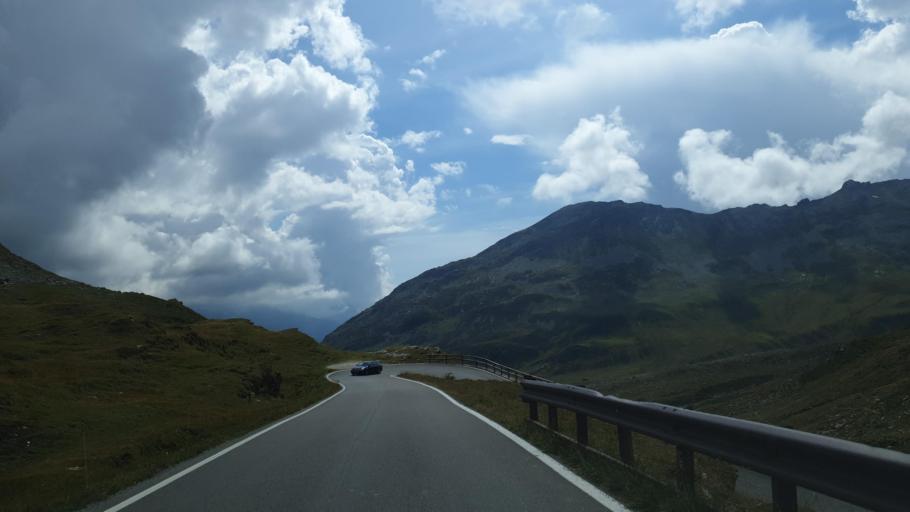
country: IT
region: Lombardy
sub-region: Provincia di Sondrio
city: Campodolcino
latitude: 46.4985
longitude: 9.3303
